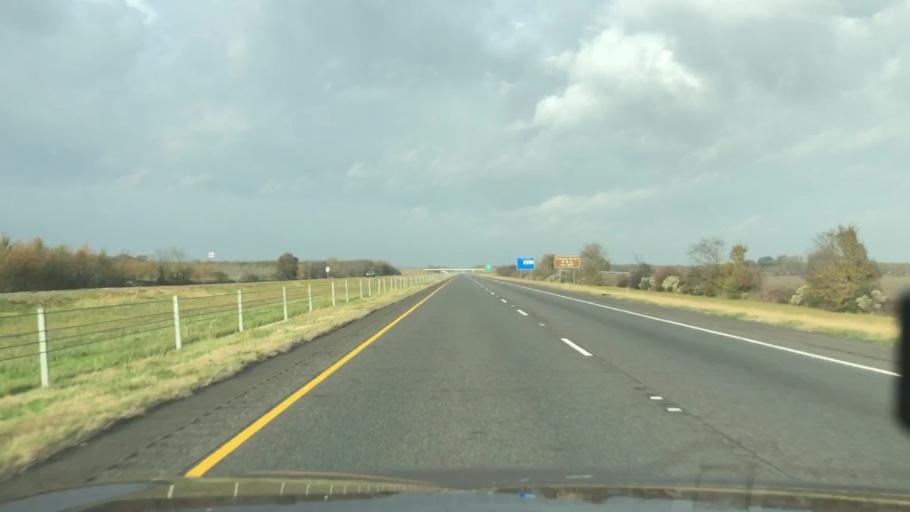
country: US
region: Louisiana
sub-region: Richland Parish
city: Delhi
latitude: 32.4298
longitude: -91.4072
